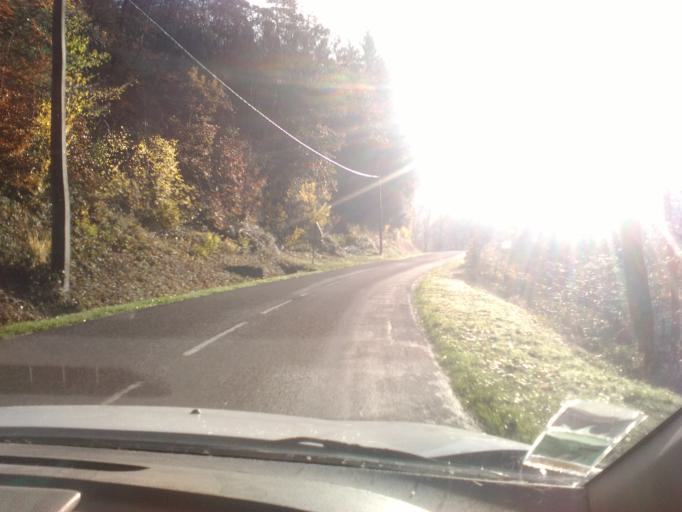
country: FR
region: Lorraine
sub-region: Departement des Vosges
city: Uzemain
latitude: 48.0678
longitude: 6.3177
